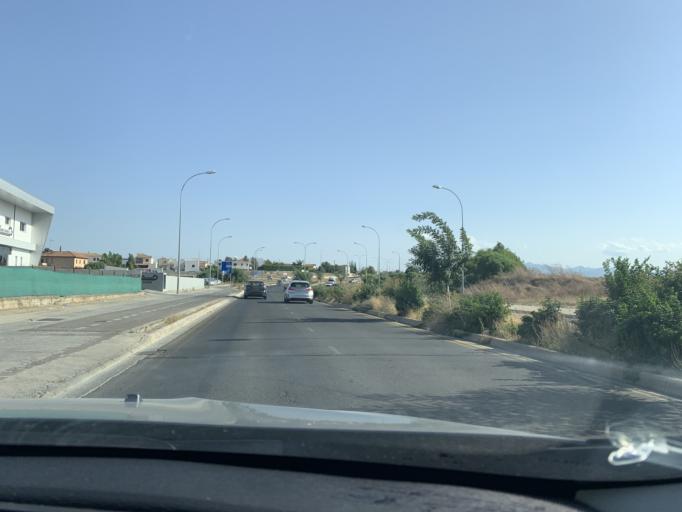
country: CY
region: Lefkosia
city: Tseri
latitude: 35.1175
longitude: 33.3566
